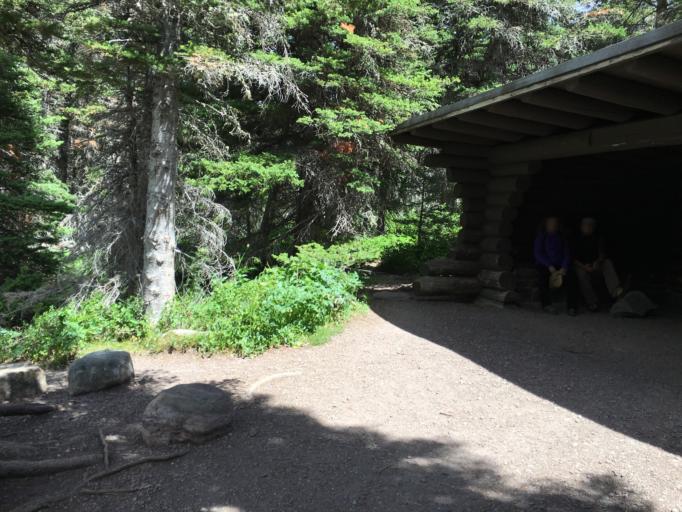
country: CA
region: Alberta
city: Cardston
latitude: 48.7748
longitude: -113.6826
